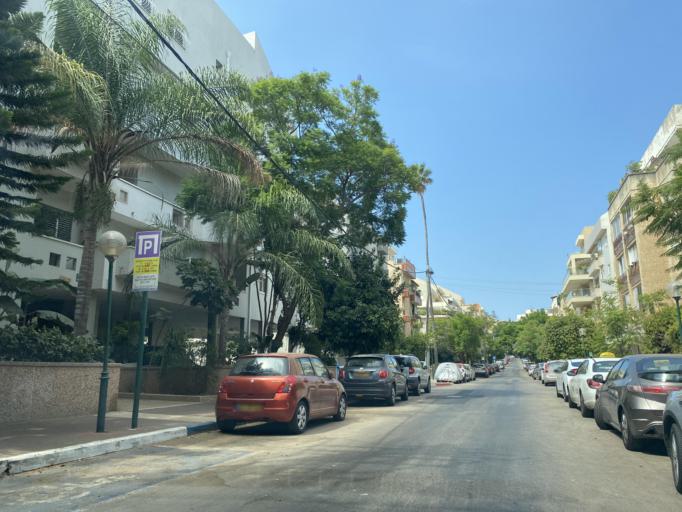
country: IL
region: Central District
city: Kfar Saba
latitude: 32.1734
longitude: 34.9078
